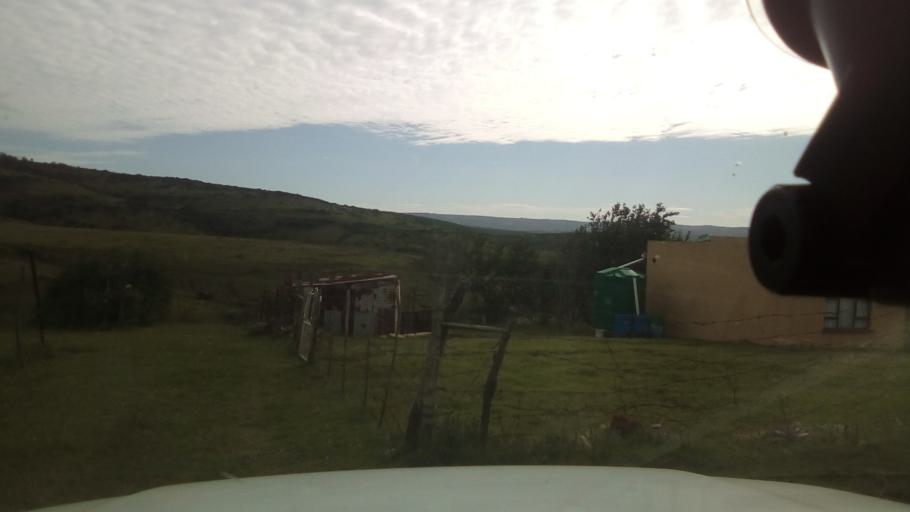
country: ZA
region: Eastern Cape
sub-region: Amathole District Municipality
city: Komga
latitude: -32.7931
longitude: 27.9579
